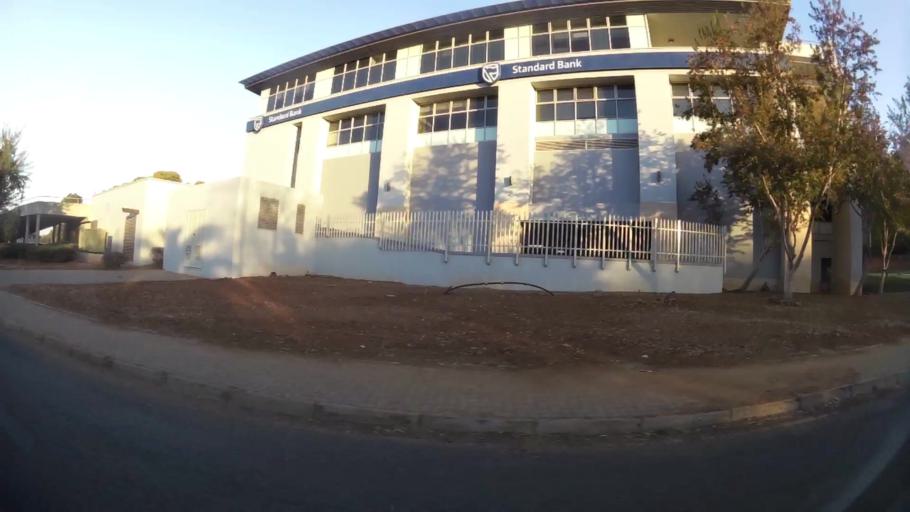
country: ZA
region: North-West
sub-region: Bojanala Platinum District Municipality
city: Rustenburg
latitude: -25.6758
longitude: 27.2470
